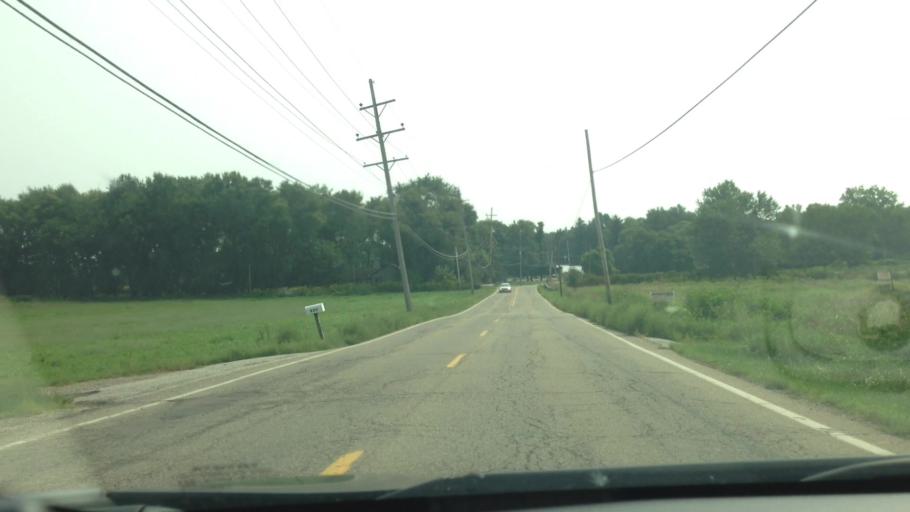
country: US
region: Ohio
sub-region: Summit County
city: Fairlawn
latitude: 41.0938
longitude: -81.5898
